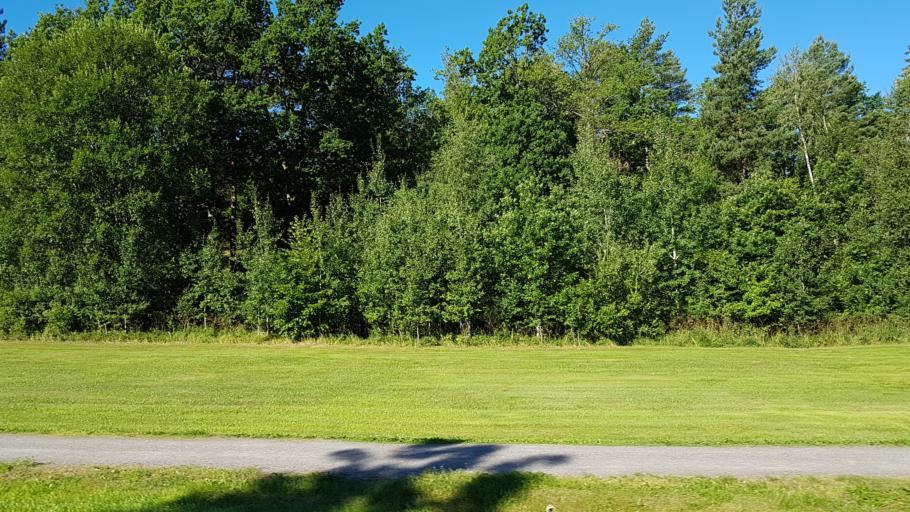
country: SE
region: OEstergoetland
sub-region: Valdemarsviks Kommun
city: Gusum
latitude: 58.4351
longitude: 16.5992
